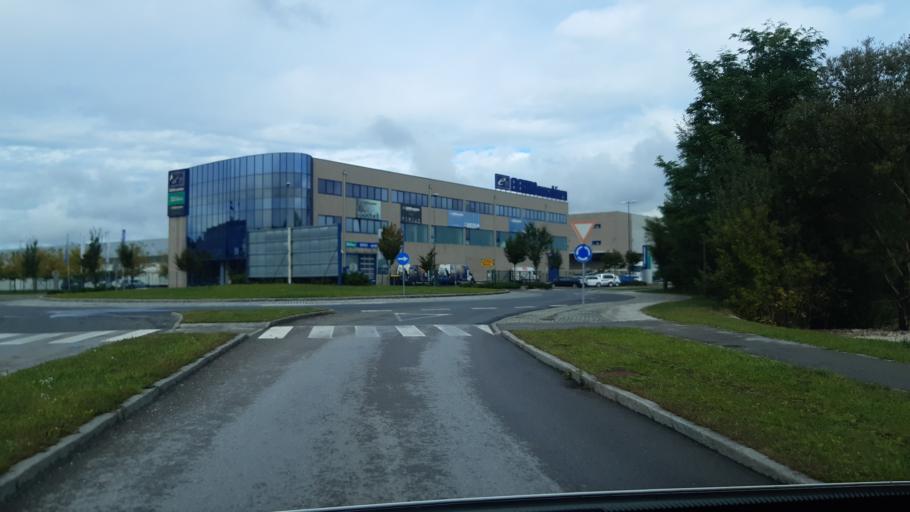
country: SI
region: Komenda
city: Komenda
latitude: 46.1894
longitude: 14.5207
